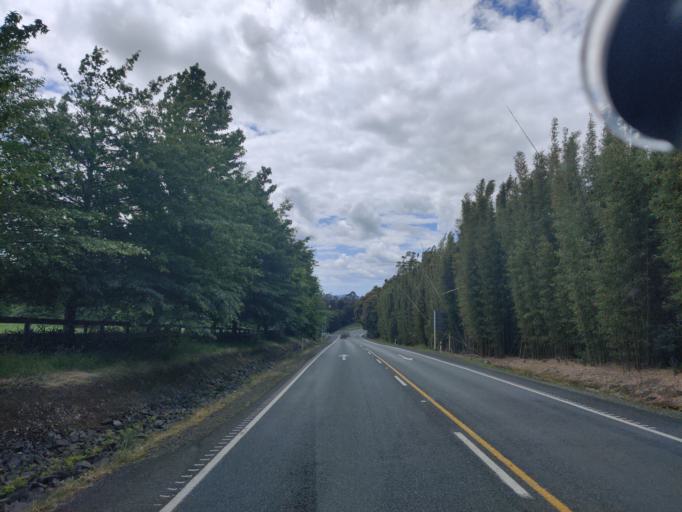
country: NZ
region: Northland
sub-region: Far North District
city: Kerikeri
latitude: -35.2522
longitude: 173.9307
